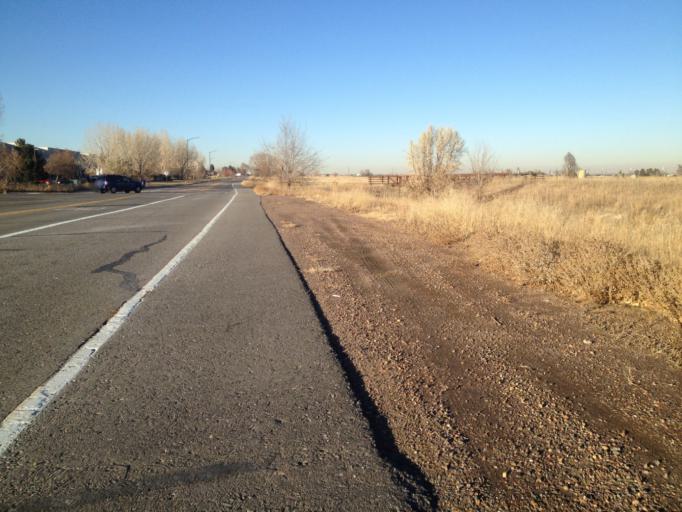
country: US
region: Colorado
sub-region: Boulder County
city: Louisville
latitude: 39.9645
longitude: -105.1093
